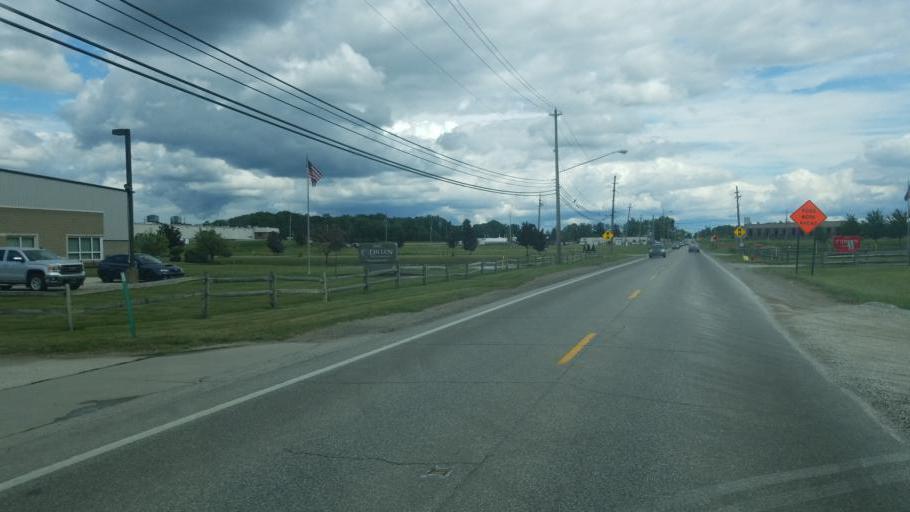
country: US
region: Ohio
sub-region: Geauga County
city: Middlefield
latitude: 41.4609
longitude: -81.0559
